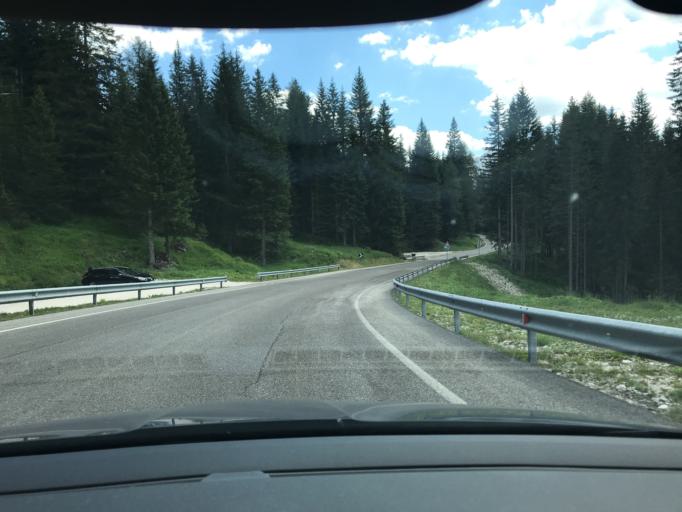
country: IT
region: Veneto
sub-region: Provincia di Belluno
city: Cortina d'Ampezzo
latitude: 46.5586
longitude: 12.2182
